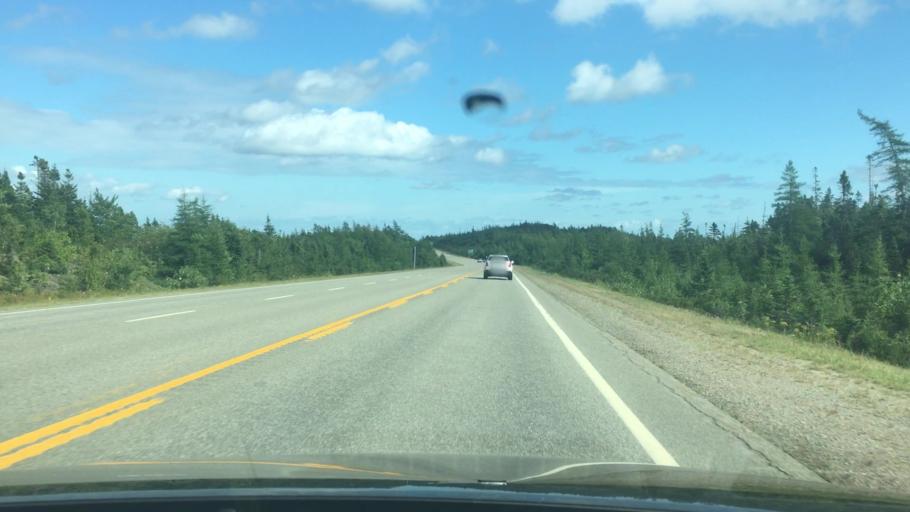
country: CA
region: Nova Scotia
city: Port Hawkesbury
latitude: 45.6169
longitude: -61.1027
